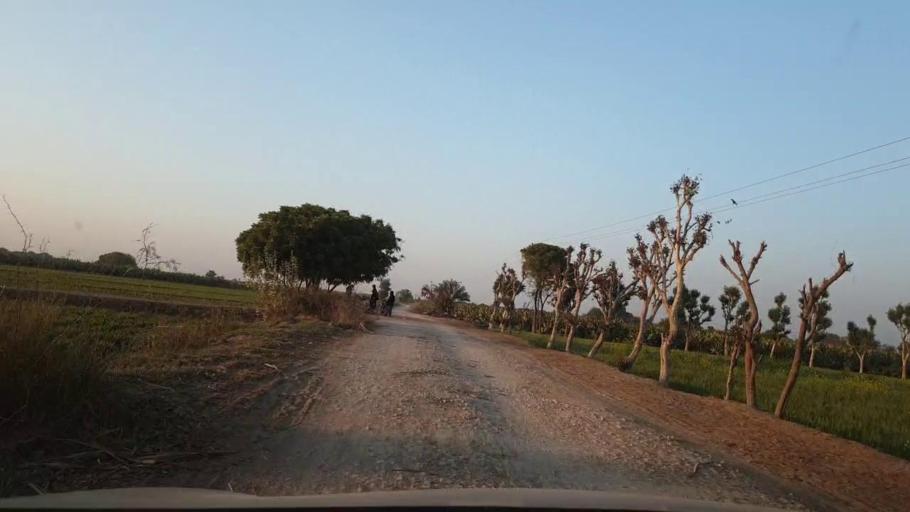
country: PK
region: Sindh
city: Tando Allahyar
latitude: 25.5129
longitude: 68.7397
